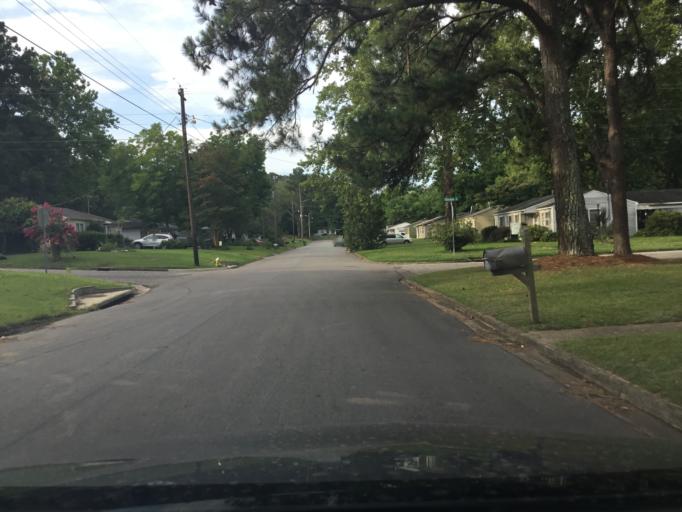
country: US
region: Alabama
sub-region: Montgomery County
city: Montgomery
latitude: 32.3628
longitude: -86.2468
